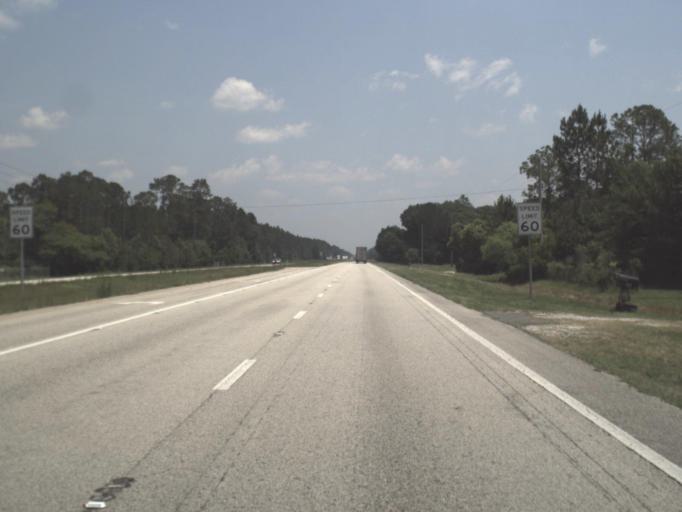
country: US
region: Florida
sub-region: Duval County
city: Baldwin
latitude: 30.2092
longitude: -82.0116
